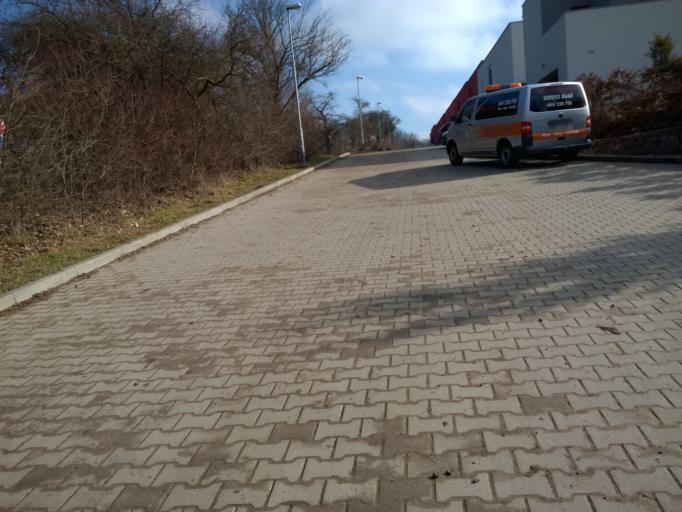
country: CZ
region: South Moravian
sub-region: Mesto Brno
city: Mokra Hora
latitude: 49.2380
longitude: 16.6013
